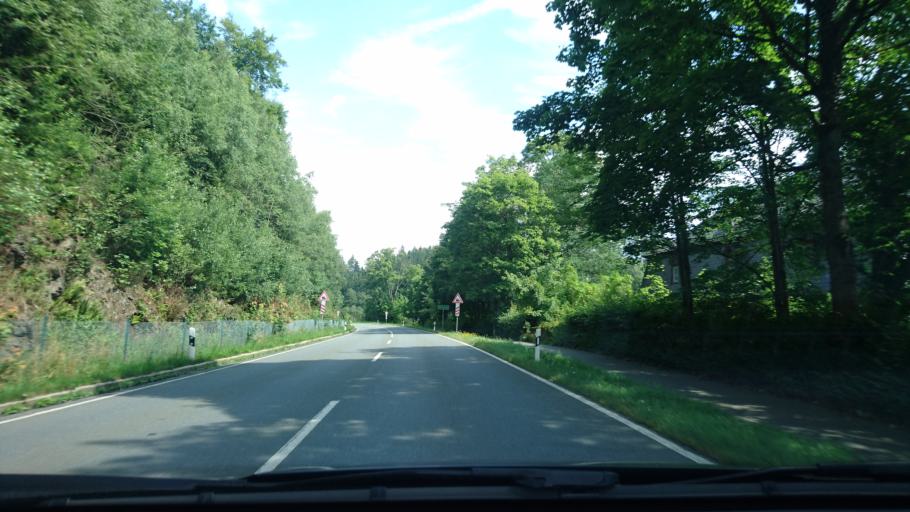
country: DE
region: Bavaria
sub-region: Upper Franconia
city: Naila
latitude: 50.3507
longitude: 11.7016
